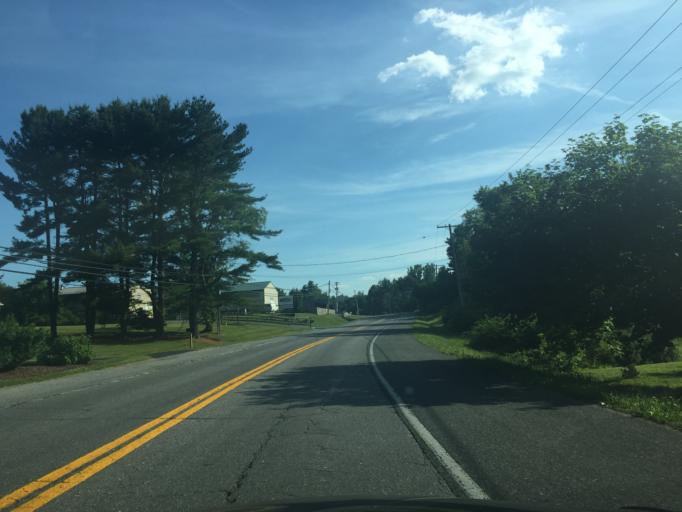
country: US
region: Maryland
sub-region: Harford County
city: Jarrettsville
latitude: 39.6343
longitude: -76.4713
